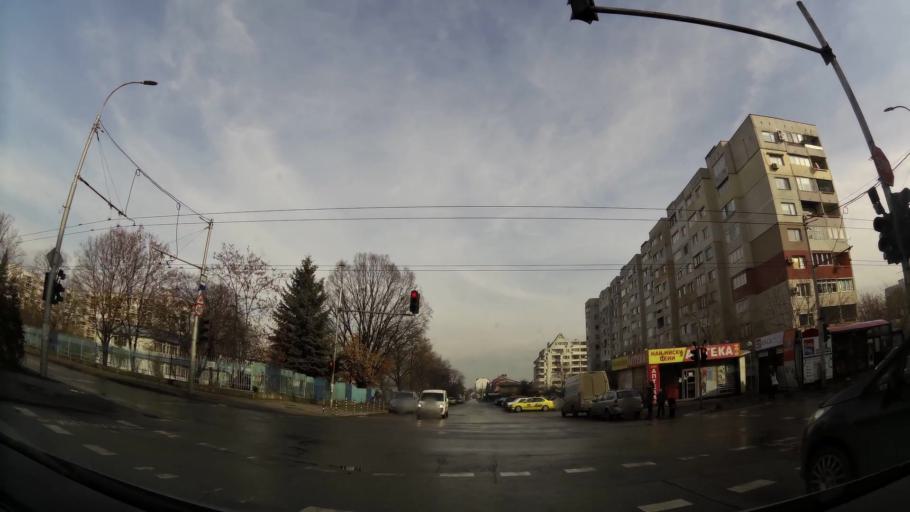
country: BG
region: Sofia-Capital
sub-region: Stolichna Obshtina
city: Sofia
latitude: 42.7210
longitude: 23.2648
